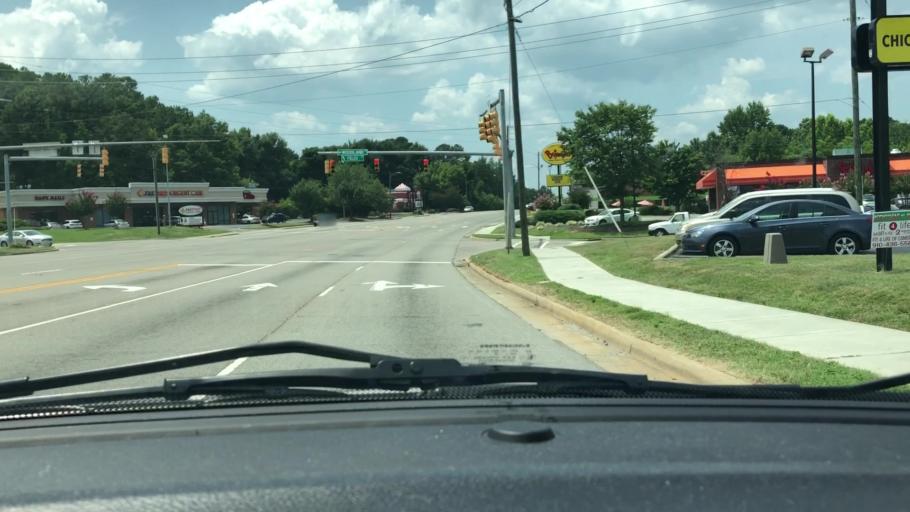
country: US
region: North Carolina
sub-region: Lee County
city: Sanford
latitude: 35.4710
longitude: -79.1721
